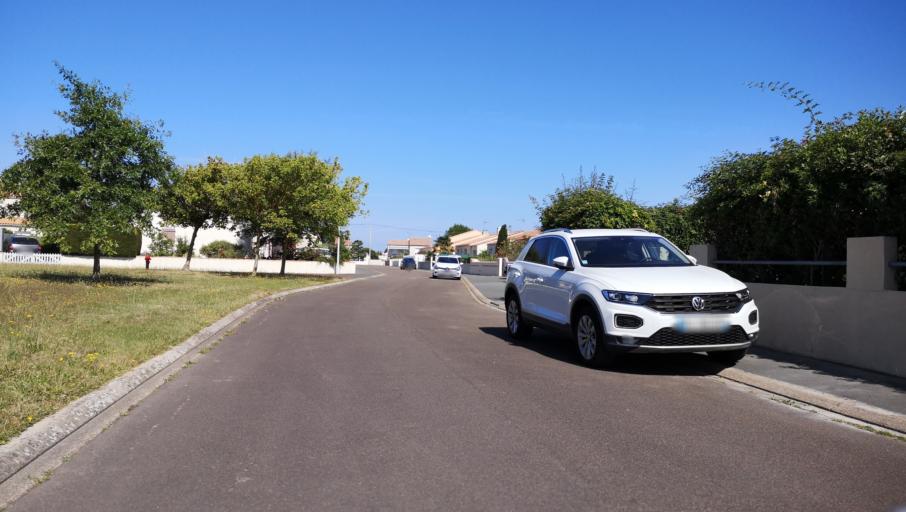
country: FR
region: Pays de la Loire
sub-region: Departement de la Vendee
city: Chateau-d'Olonne
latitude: 46.4930
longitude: -1.7518
